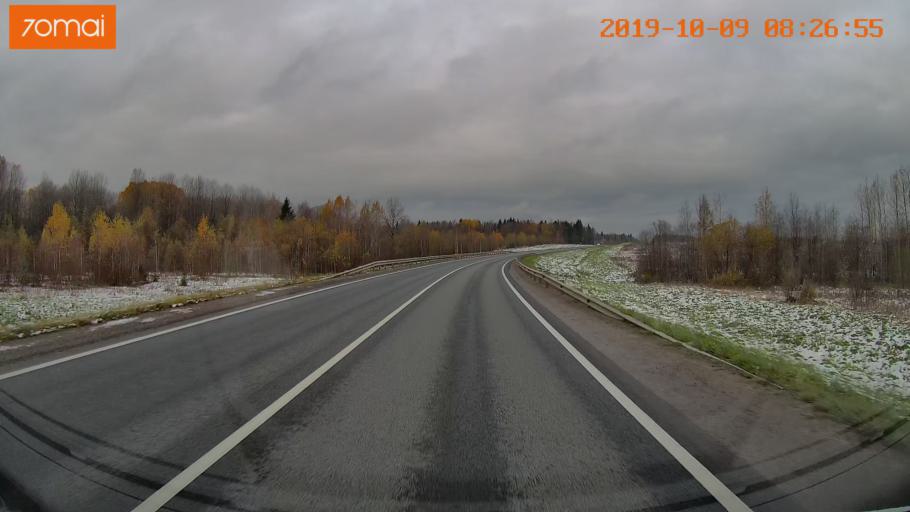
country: RU
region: Vologda
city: Gryazovets
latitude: 58.7980
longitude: 40.2578
